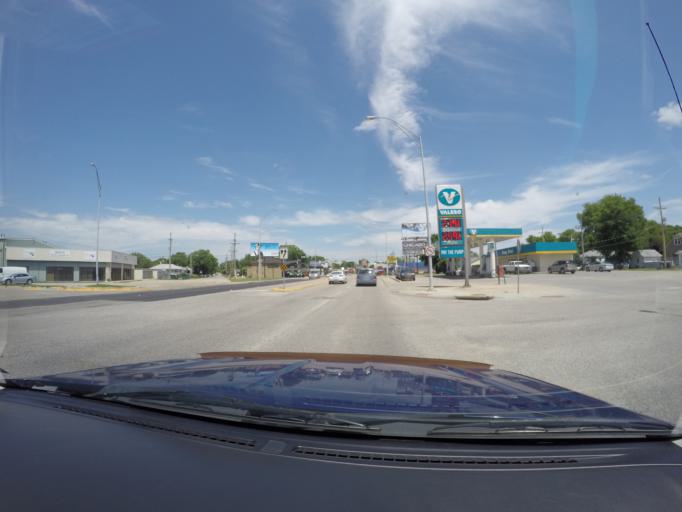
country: US
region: Nebraska
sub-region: Hall County
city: Grand Island
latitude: 40.9156
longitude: -98.3397
